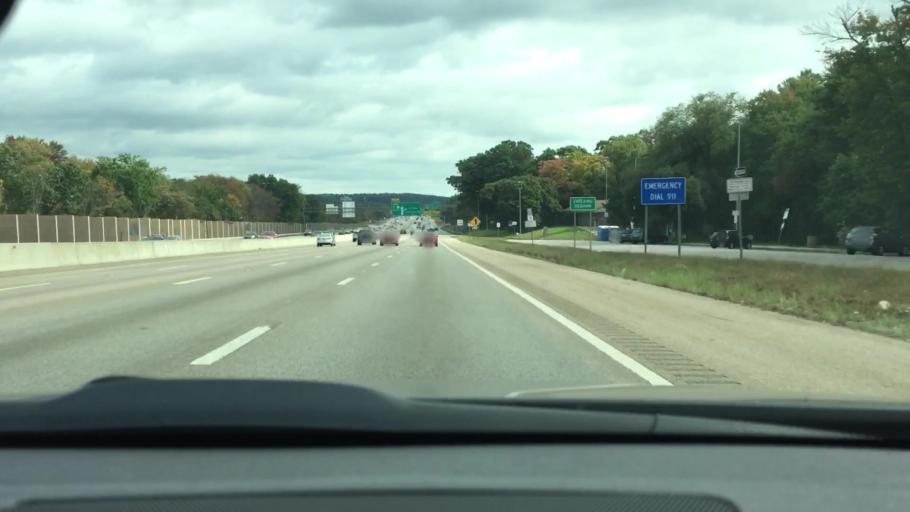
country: US
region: Massachusetts
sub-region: Norfolk County
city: Dedham
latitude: 42.2181
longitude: -71.1591
